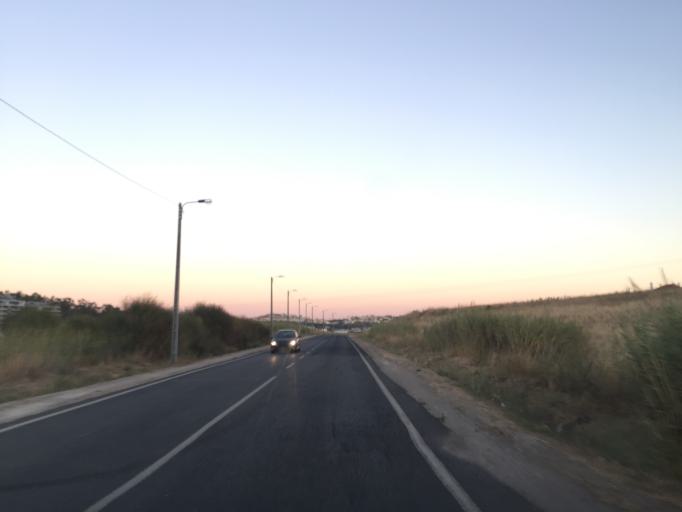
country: PT
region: Lisbon
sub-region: Odivelas
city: Povoa de Santo Adriao
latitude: 38.8103
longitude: -9.1730
